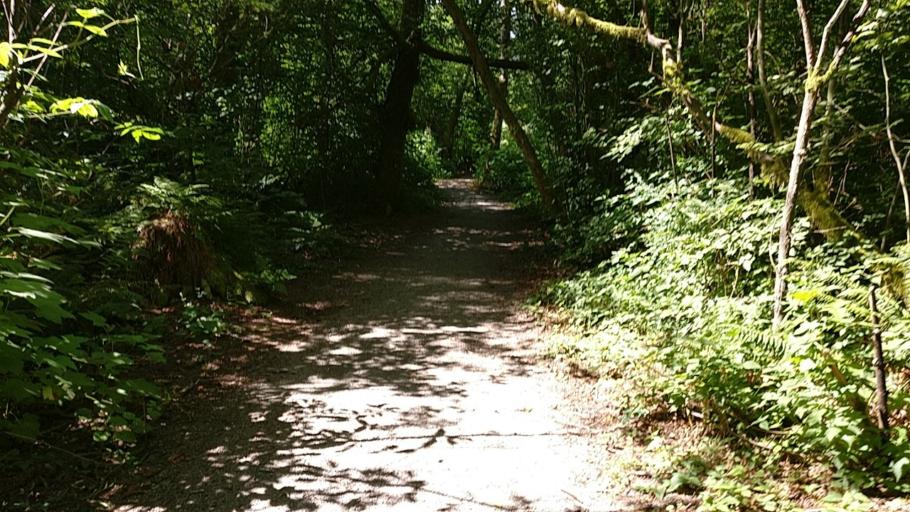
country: CA
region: British Columbia
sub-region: Greater Vancouver Regional District
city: White Rock
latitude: 49.0490
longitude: -122.8610
